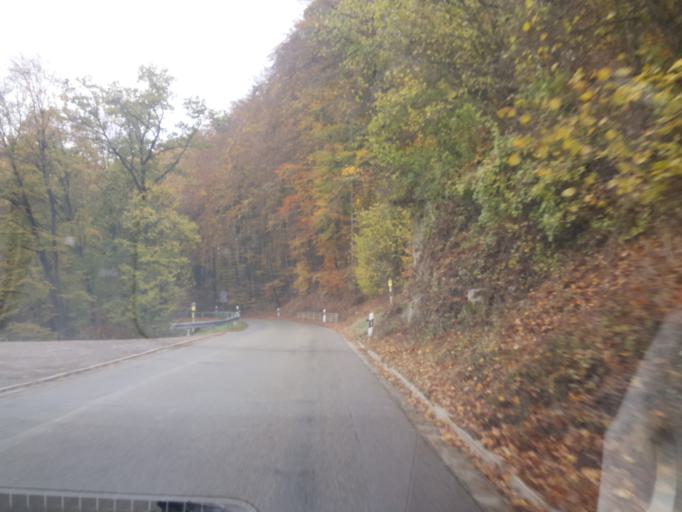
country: DE
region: Bavaria
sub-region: Upper Bavaria
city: Rennertshofen
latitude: 48.8208
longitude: 11.0798
